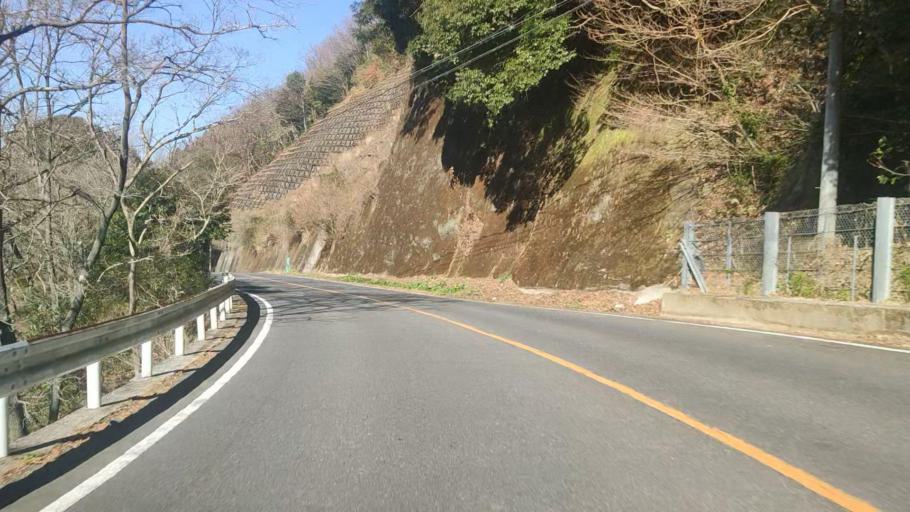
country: JP
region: Oita
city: Saiki
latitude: 32.8881
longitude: 131.9436
